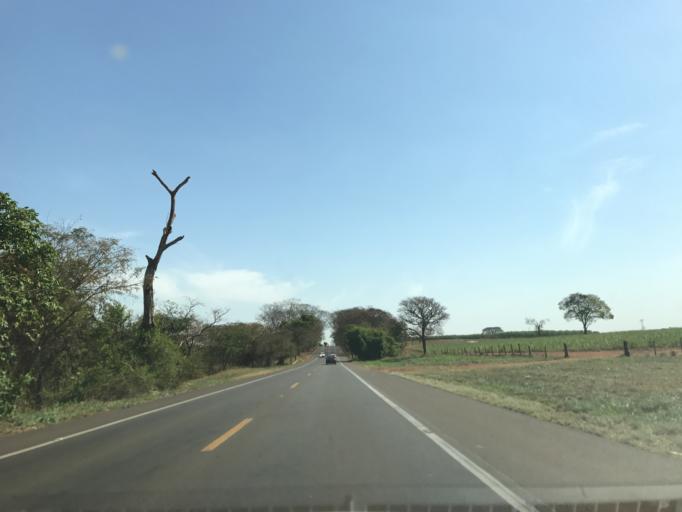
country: BR
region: Sao Paulo
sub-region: Jose Bonifacio
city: Jose Bonifacio
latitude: -21.0242
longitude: -49.6681
